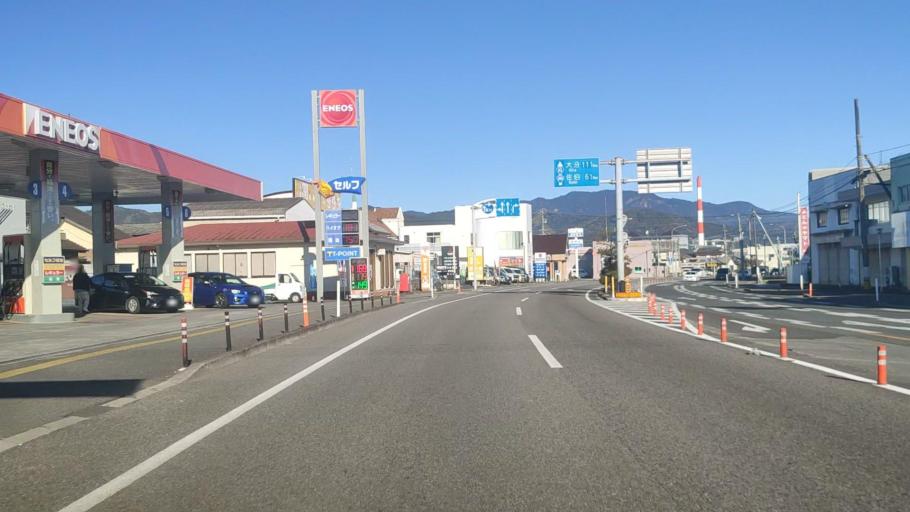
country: JP
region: Miyazaki
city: Nobeoka
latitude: 32.5900
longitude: 131.6758
